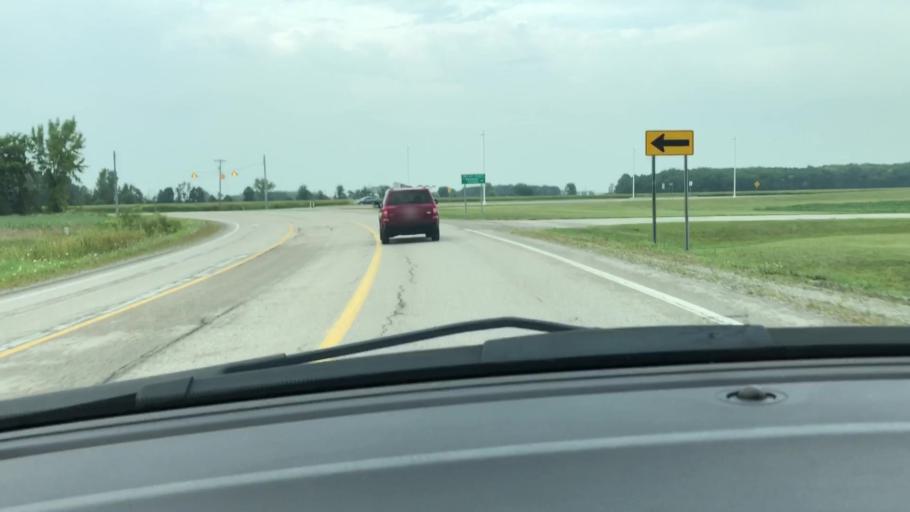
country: US
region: Michigan
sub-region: Saginaw County
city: Freeland
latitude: 43.5413
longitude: -84.0912
